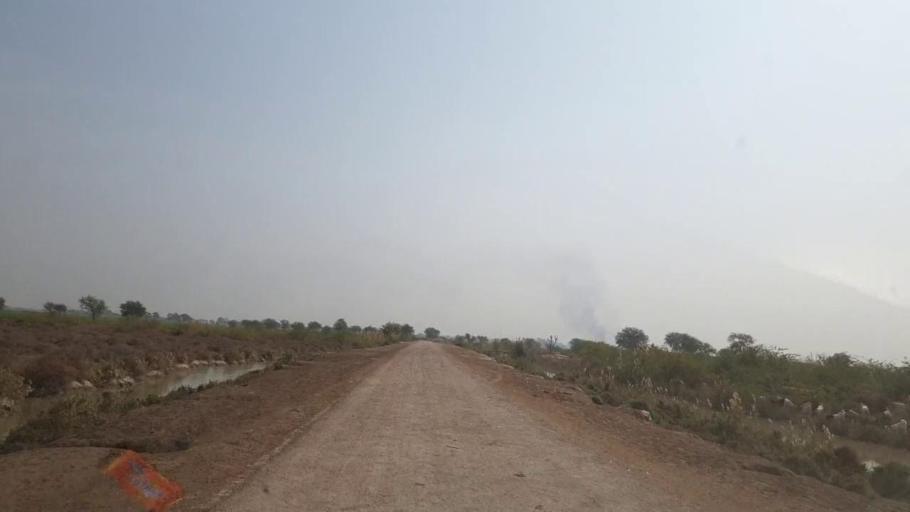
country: PK
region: Sindh
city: Mirpur Khas
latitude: 25.5354
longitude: 69.0637
